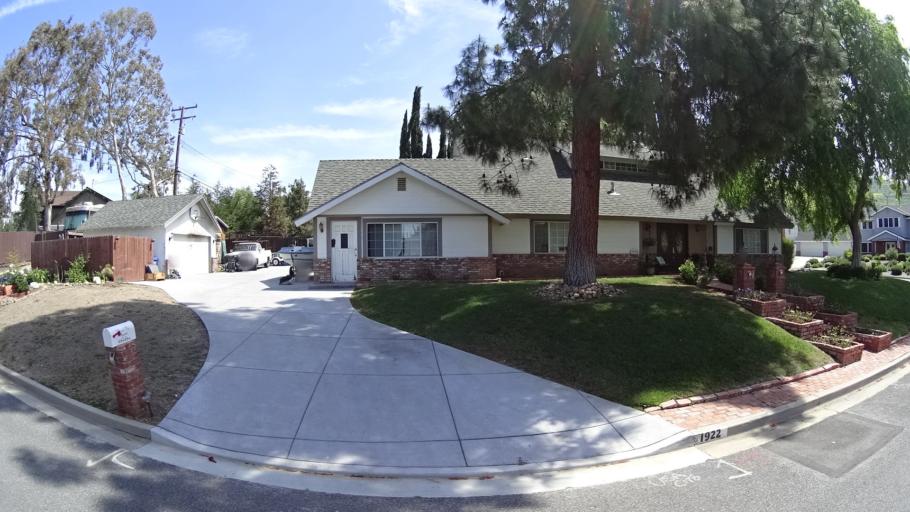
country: US
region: California
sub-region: Ventura County
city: Thousand Oaks
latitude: 34.2037
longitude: -118.8441
